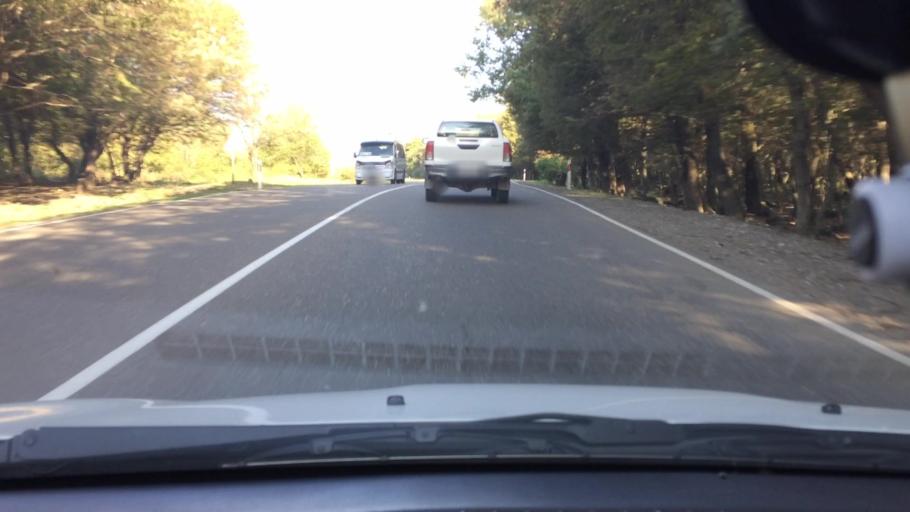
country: GE
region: Imereti
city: Kutaisi
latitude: 42.2288
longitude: 42.7796
